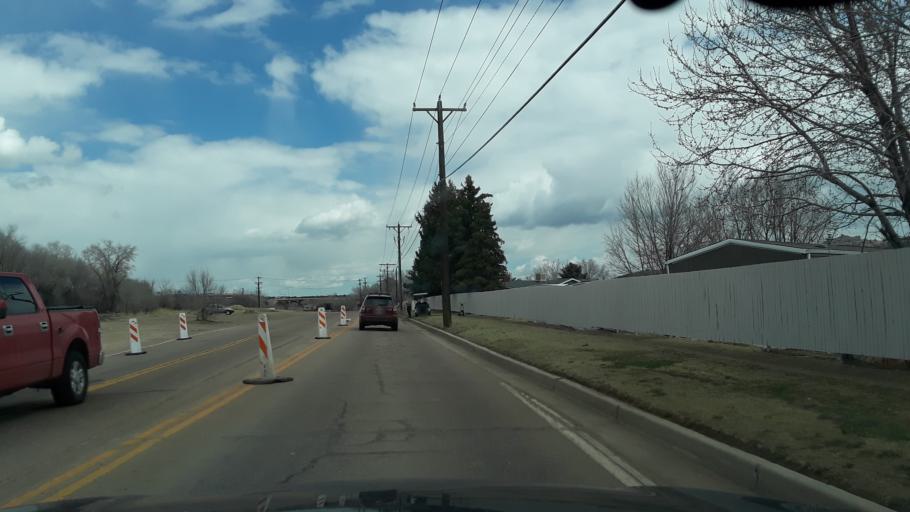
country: US
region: Colorado
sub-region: El Paso County
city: Colorado Springs
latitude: 38.9005
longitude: -104.8247
